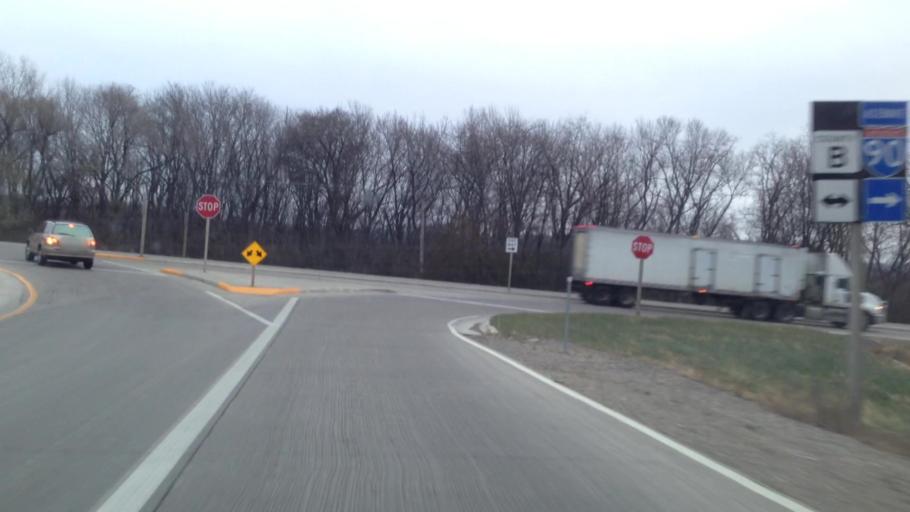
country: US
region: Wisconsin
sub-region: La Crosse County
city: French Island
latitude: 43.8596
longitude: -91.2563
